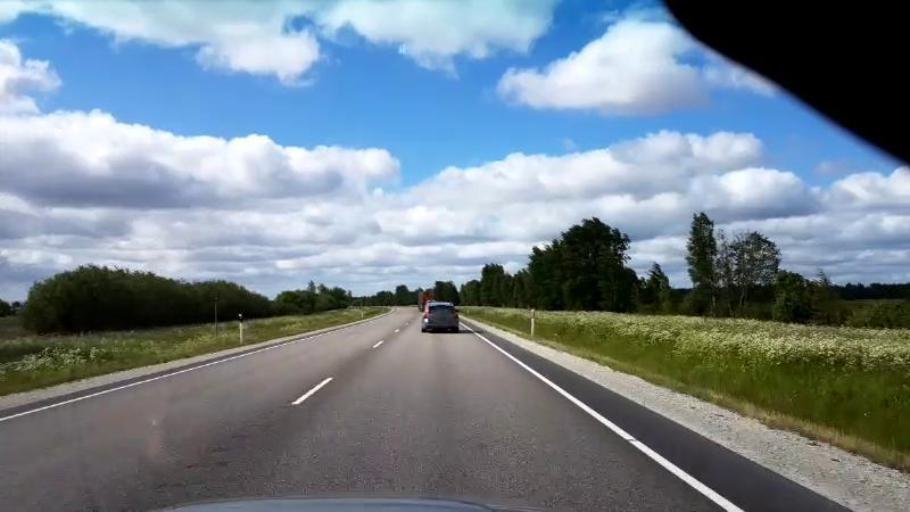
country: EE
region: Paernumaa
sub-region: Sauga vald
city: Sauga
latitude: 58.4957
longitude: 24.5334
